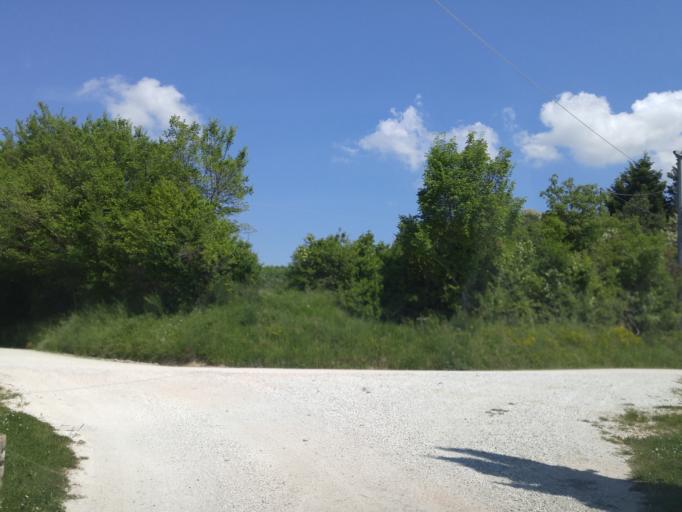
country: IT
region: The Marches
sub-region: Provincia di Pesaro e Urbino
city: Fermignano
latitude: 43.6993
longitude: 12.6452
